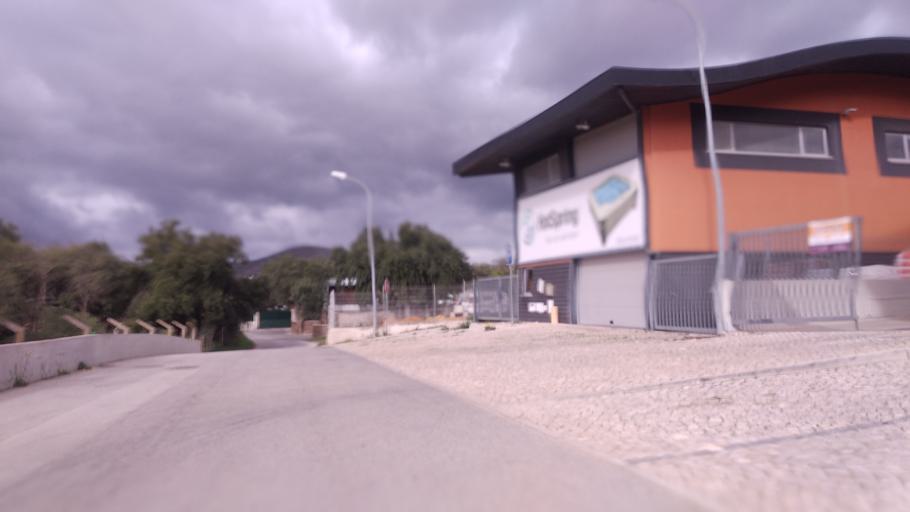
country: PT
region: Faro
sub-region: Loule
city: Almancil
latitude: 37.0976
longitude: -8.0452
